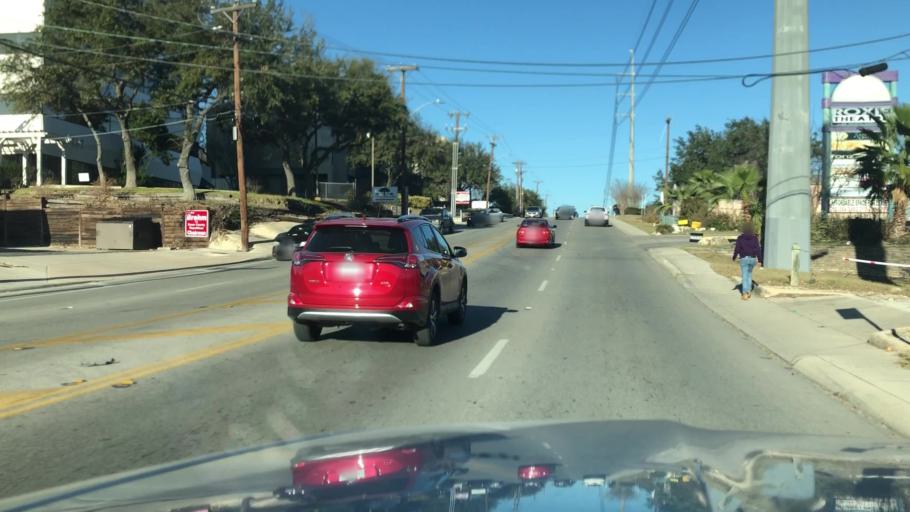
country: US
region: Texas
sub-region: Bexar County
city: Balcones Heights
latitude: 29.5037
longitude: -98.5598
